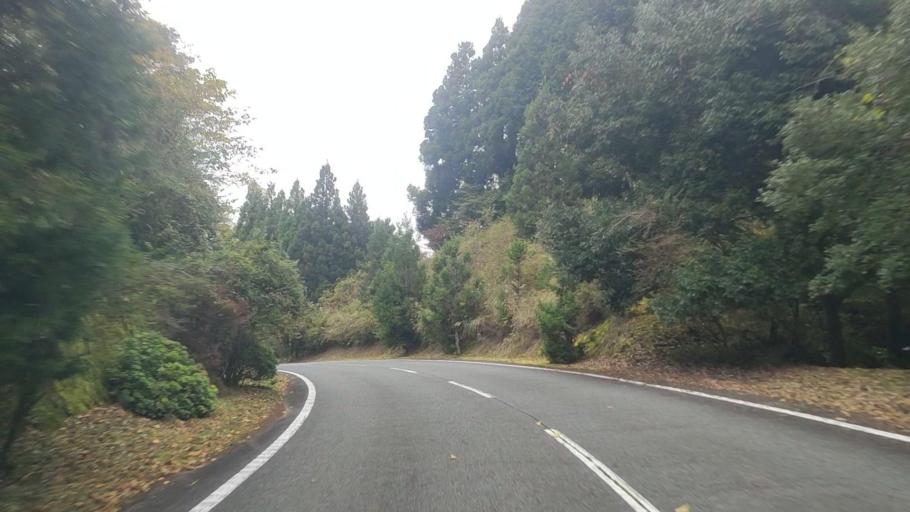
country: JP
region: Shizuoka
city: Heda
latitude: 34.9124
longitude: 138.8481
